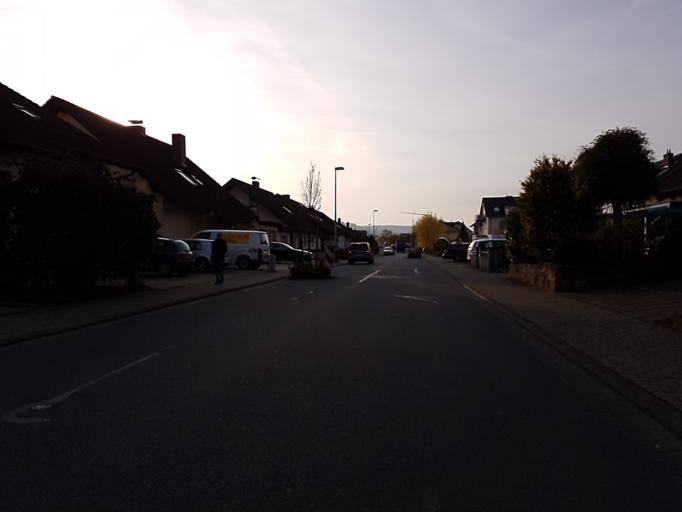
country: DE
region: Bavaria
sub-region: Regierungsbezirk Unterfranken
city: Grosswallstadt
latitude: 49.8853
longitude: 9.1579
